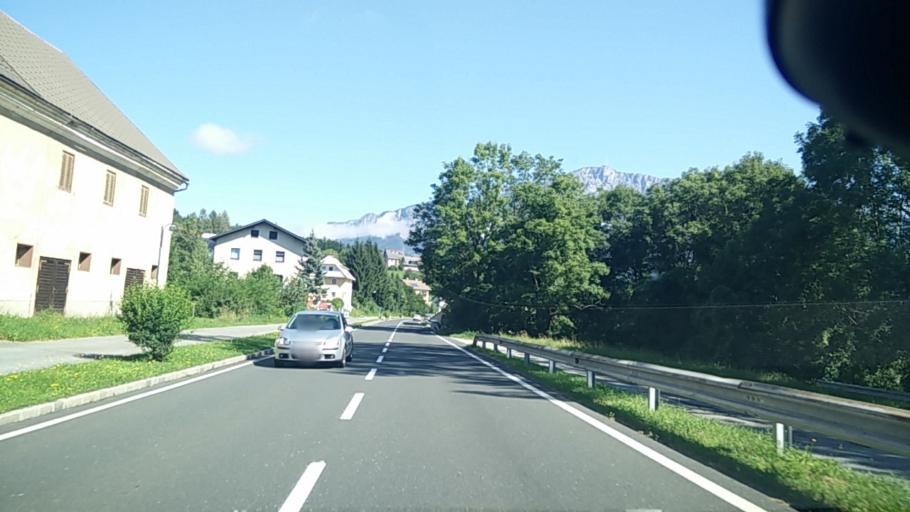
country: AT
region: Carinthia
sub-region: Politischer Bezirk Villach Land
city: Hohenthurn
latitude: 46.5387
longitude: 13.6447
